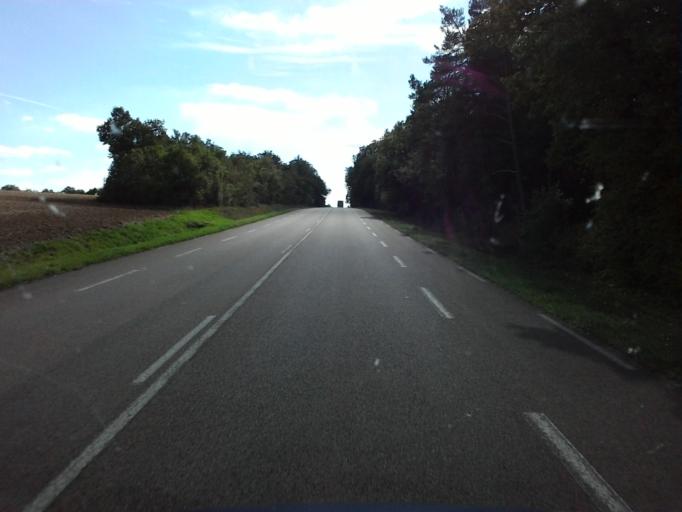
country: FR
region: Bourgogne
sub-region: Departement de la Cote-d'Or
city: Chatillon-sur-Seine
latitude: 47.8230
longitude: 4.5386
